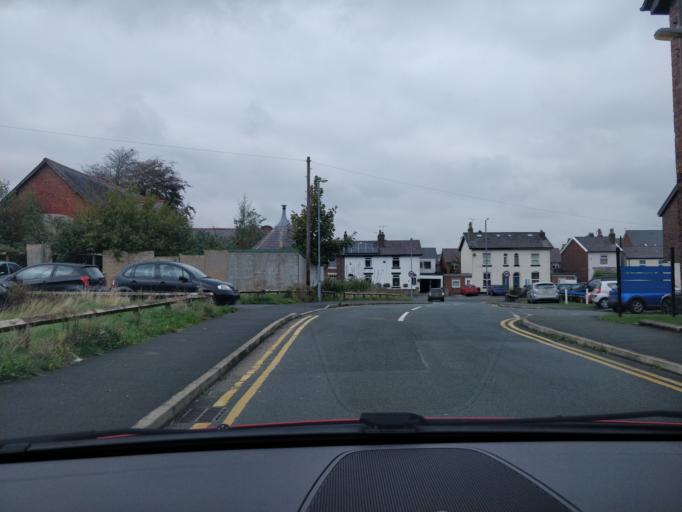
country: GB
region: England
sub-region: Lancashire
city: Ormskirk
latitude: 53.5662
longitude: -2.8767
